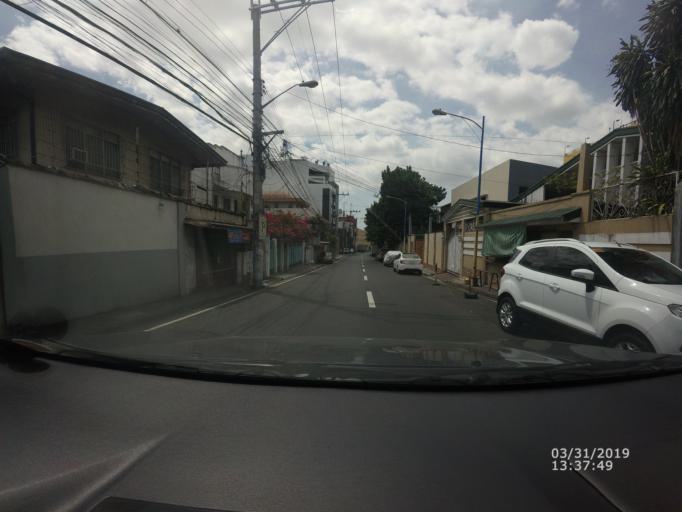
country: PH
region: Metro Manila
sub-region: Mandaluyong
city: Mandaluyong City
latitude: 14.5830
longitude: 121.0479
